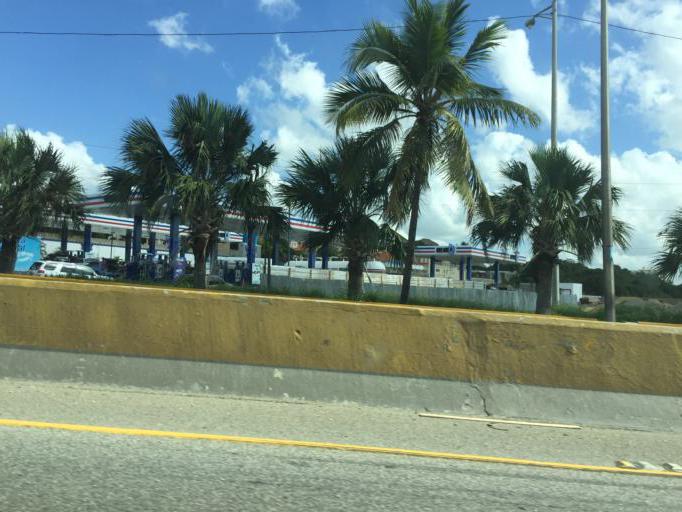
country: DO
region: Santo Domingo
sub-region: Santo Domingo
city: Santo Domingo Este
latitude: 18.4761
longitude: -69.8352
